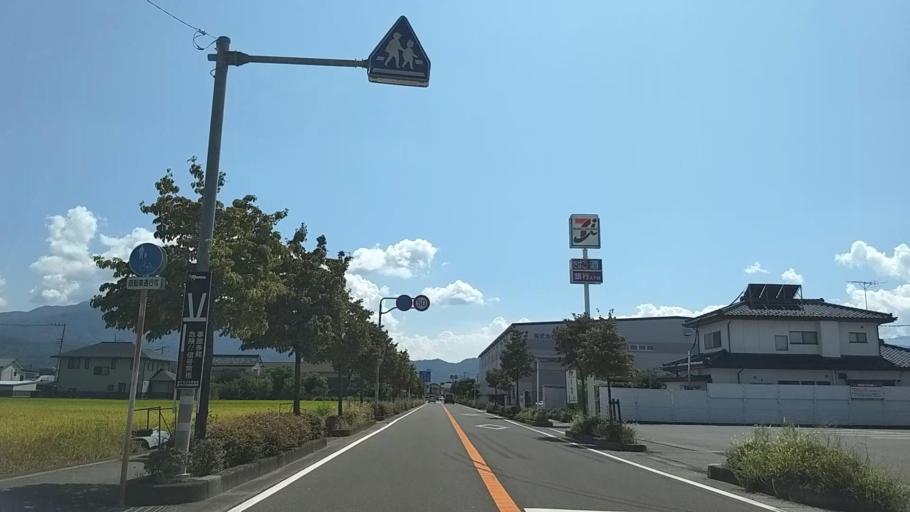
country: JP
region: Yamanashi
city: Ryuo
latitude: 35.5967
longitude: 138.5037
